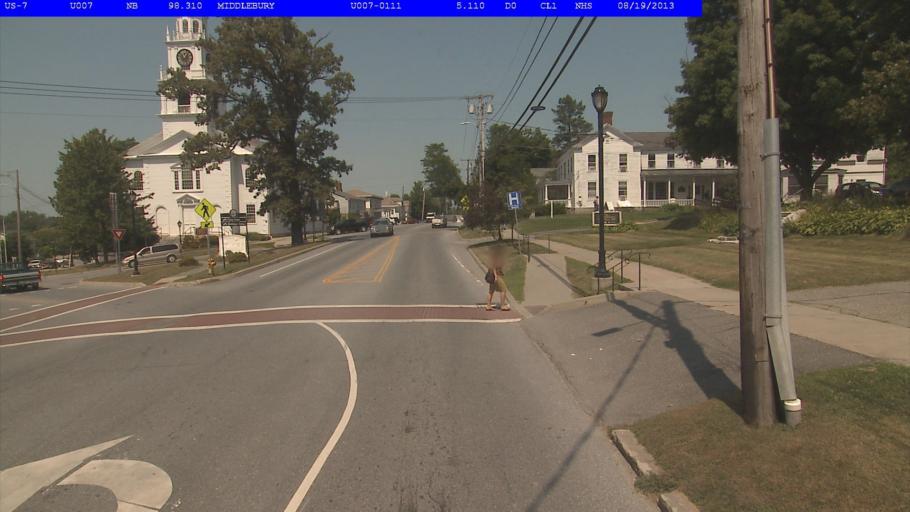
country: US
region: Vermont
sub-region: Addison County
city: Middlebury (village)
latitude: 44.0146
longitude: -73.1667
